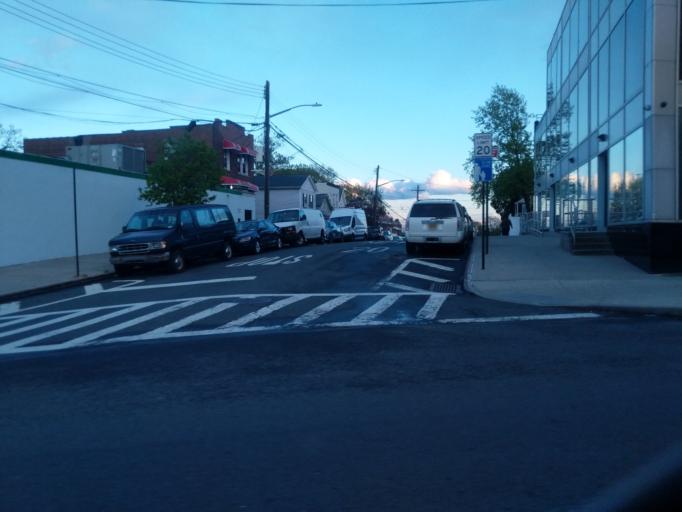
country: US
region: New York
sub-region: Bronx
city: Eastchester
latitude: 40.8790
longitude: -73.8435
